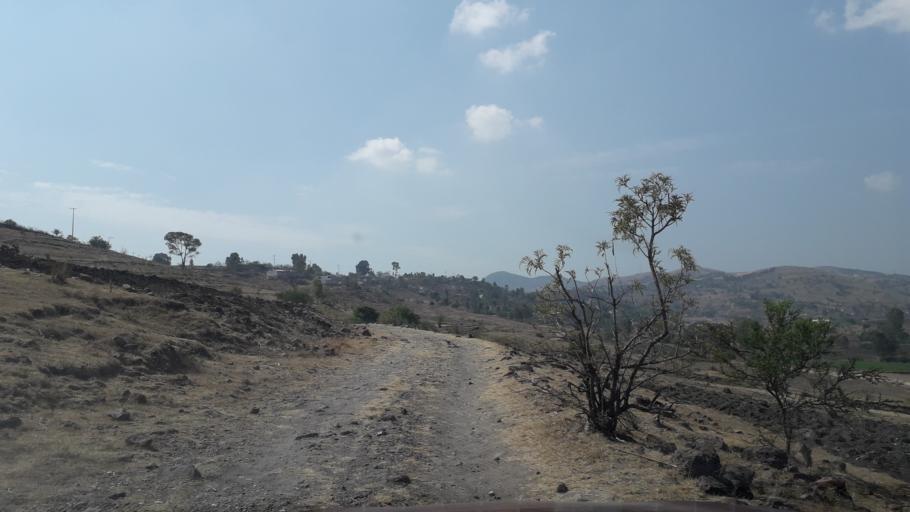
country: MX
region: Puebla
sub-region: Puebla
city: San Andres Azumiatla
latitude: 18.9142
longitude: -98.2594
